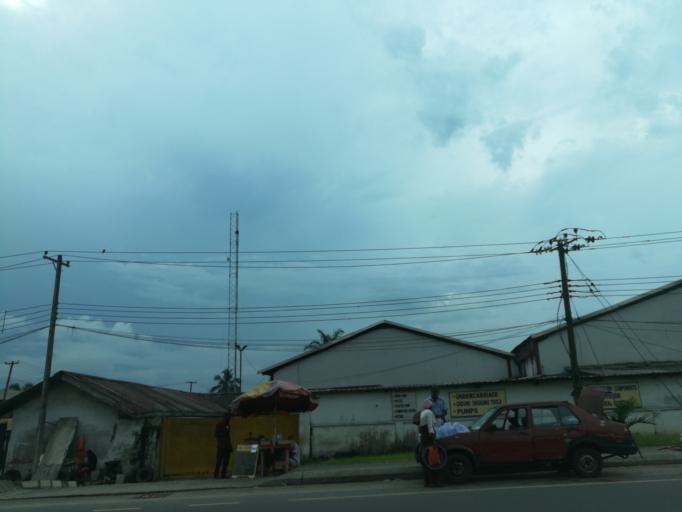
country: NG
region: Rivers
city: Port Harcourt
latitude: 4.8092
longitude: 7.0135
